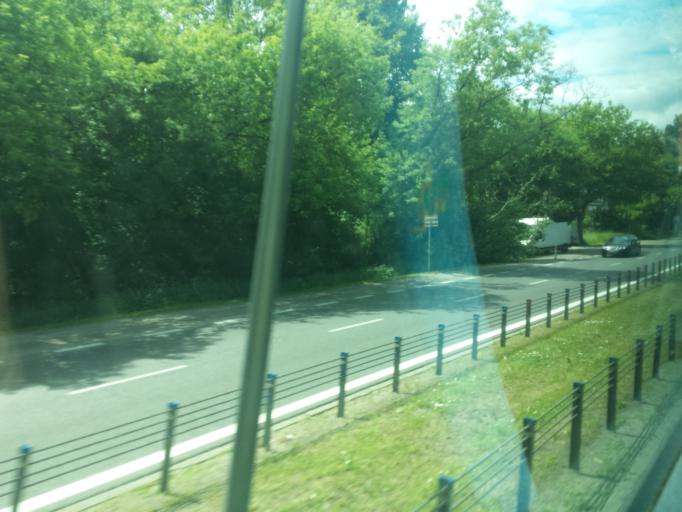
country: PL
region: Masovian Voivodeship
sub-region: Warszawa
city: Wawer
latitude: 52.2254
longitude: 21.1764
